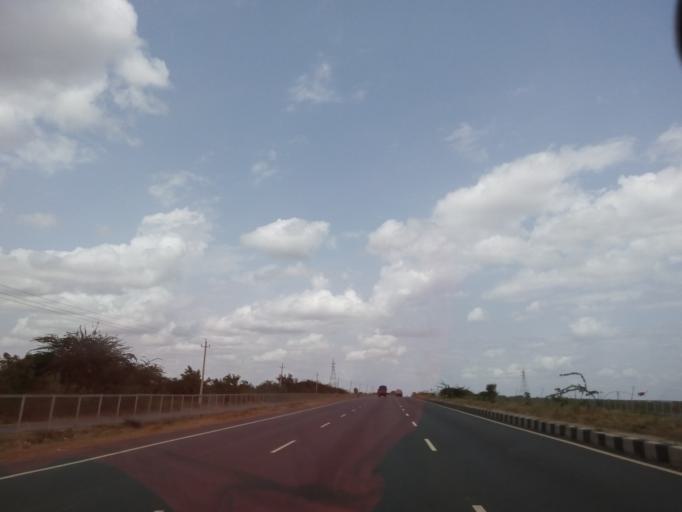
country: IN
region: Karnataka
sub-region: Chitradurga
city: Hiriyur
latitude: 13.8669
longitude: 76.7070
